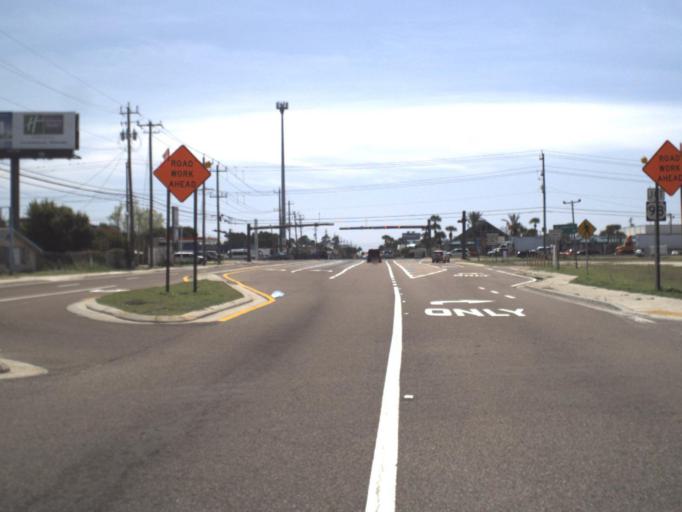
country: US
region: Florida
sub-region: Bay County
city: Laguna Beach
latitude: 30.2316
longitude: -85.8872
